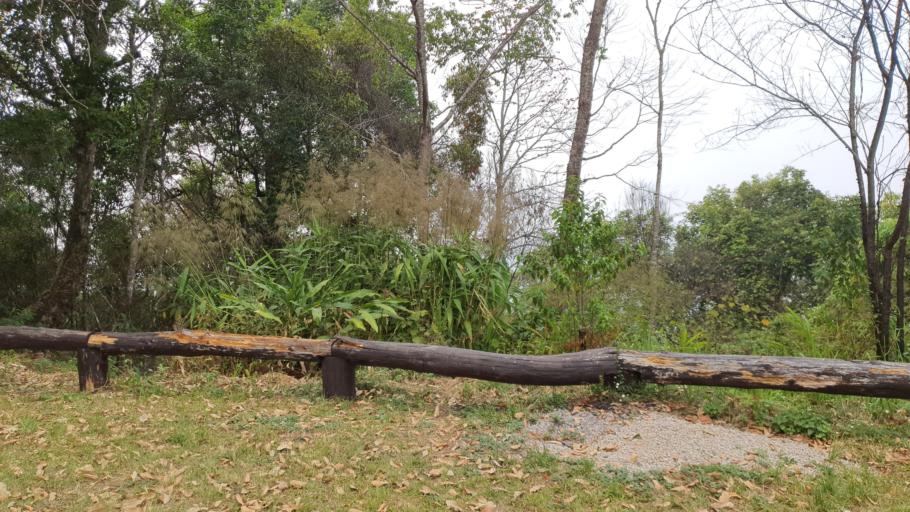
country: TH
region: Chiang Mai
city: Chiang Mai
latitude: 18.8342
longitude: 98.8880
